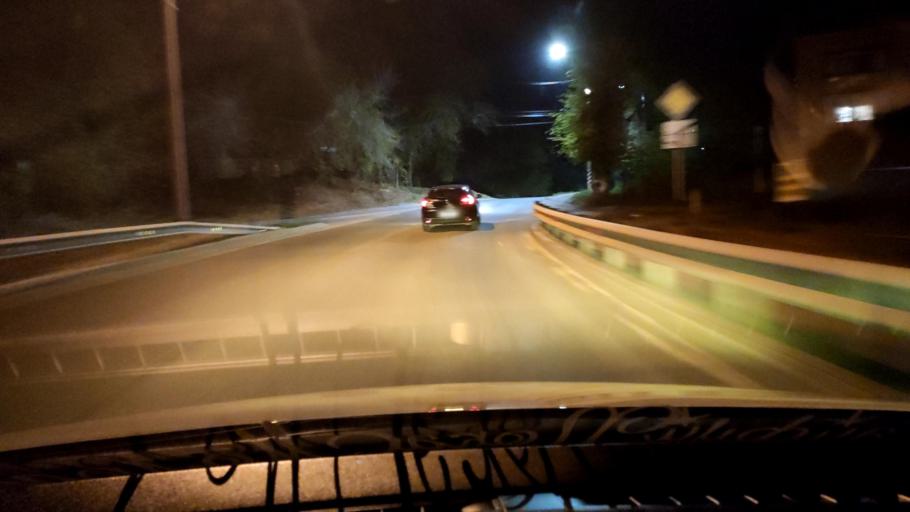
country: RU
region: Voronezj
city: Semiluki
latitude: 51.6770
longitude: 39.0304
